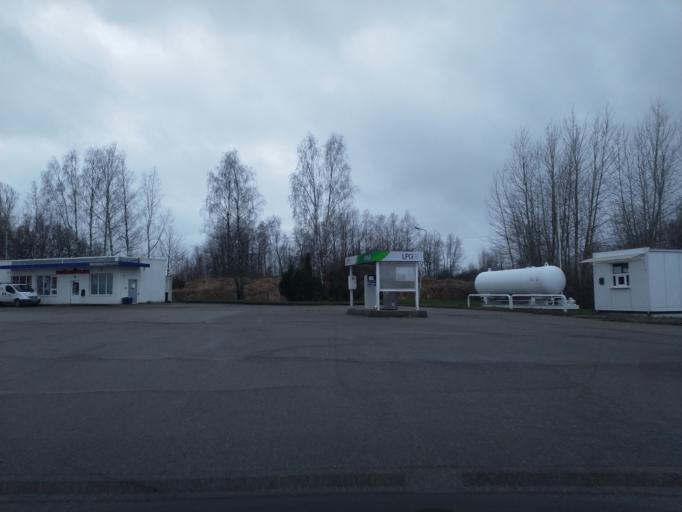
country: LV
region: Kuldigas Rajons
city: Kuldiga
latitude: 56.9538
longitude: 21.9916
